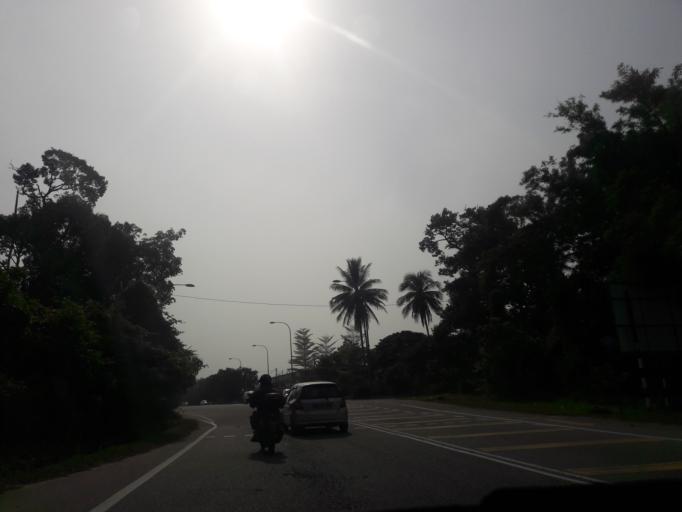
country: MY
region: Kedah
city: Kulim
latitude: 5.3499
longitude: 100.5261
